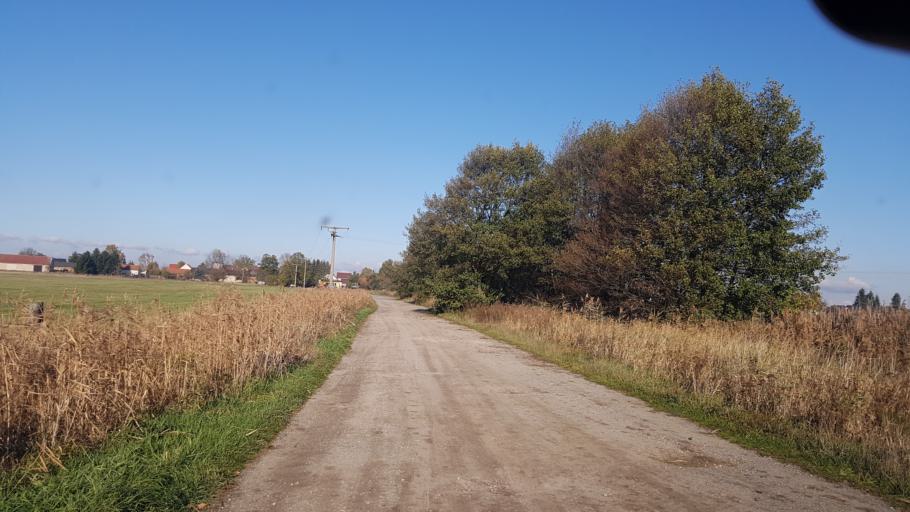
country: DE
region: Brandenburg
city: Ruckersdorf
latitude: 51.5600
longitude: 13.5436
